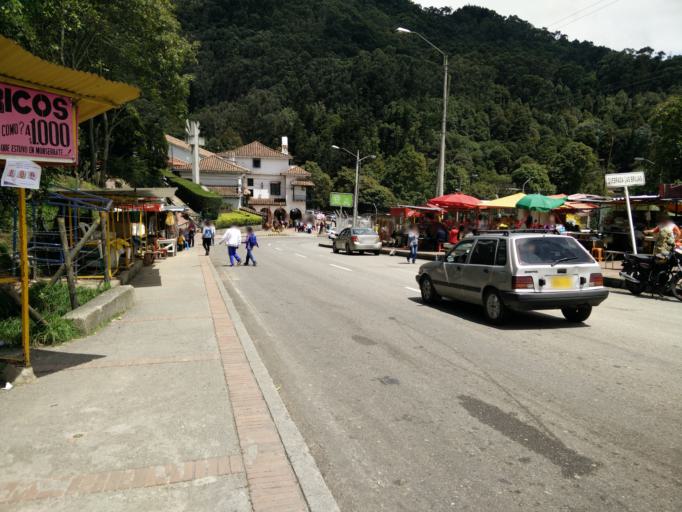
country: CO
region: Bogota D.C.
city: Bogota
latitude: 4.6037
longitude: -74.0615
